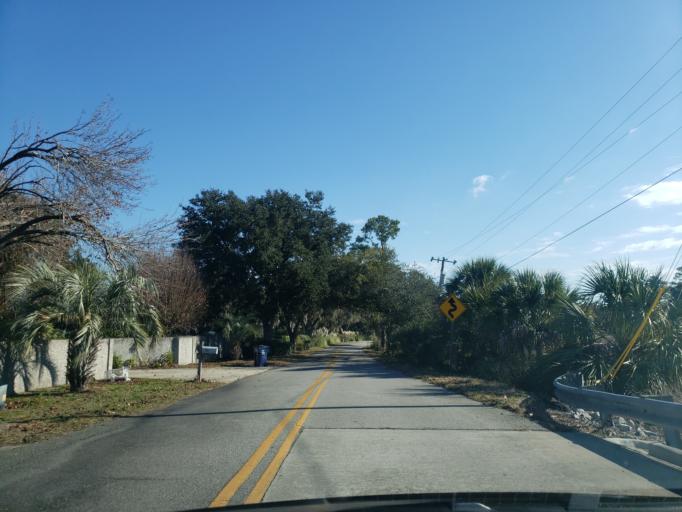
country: US
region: Georgia
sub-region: Chatham County
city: Whitemarsh Island
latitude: 32.0526
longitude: -81.0115
